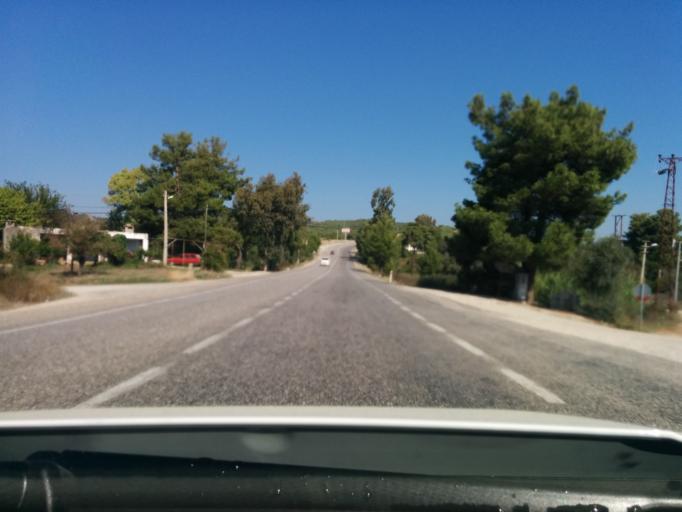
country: TR
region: Mugla
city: Kemer
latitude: 36.5931
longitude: 29.3507
